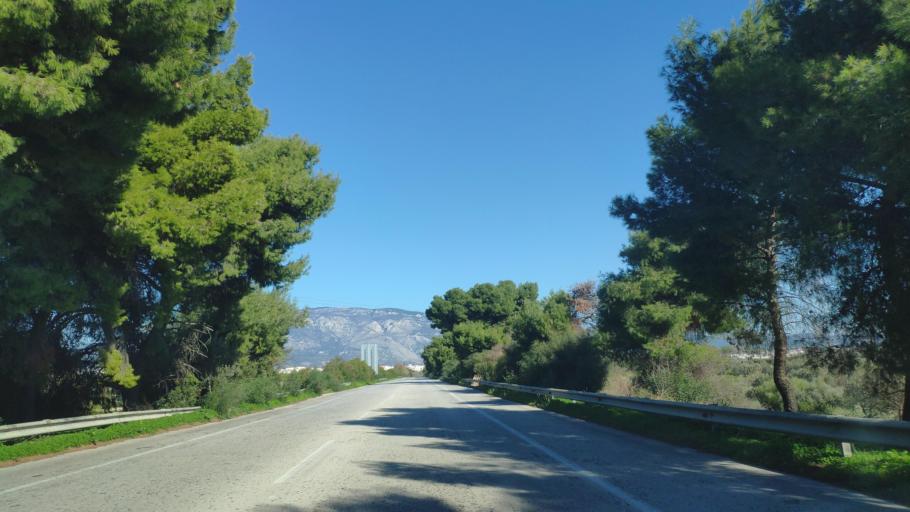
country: GR
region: Peloponnese
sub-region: Nomos Korinthias
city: Examilia
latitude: 37.9244
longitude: 22.9148
